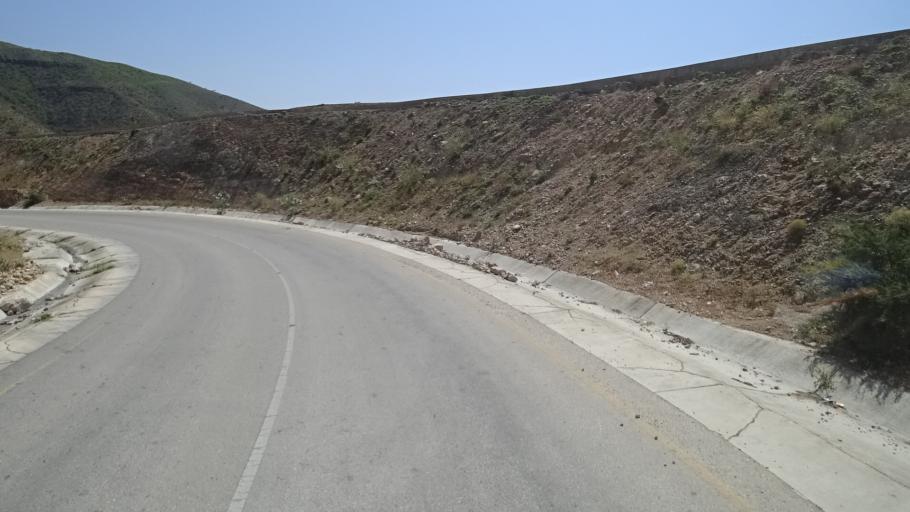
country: OM
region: Zufar
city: Salalah
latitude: 17.0463
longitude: 54.6118
